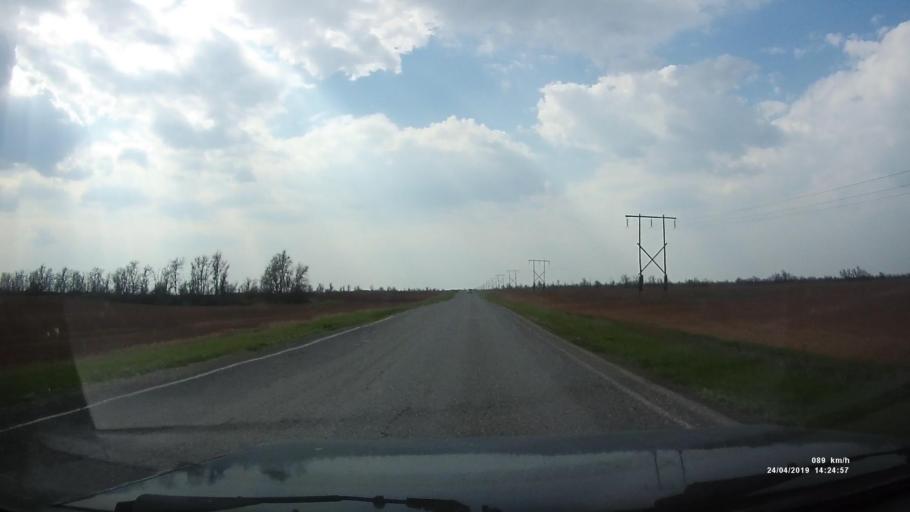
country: RU
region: Kalmykiya
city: Arshan'
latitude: 46.3295
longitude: 44.0880
